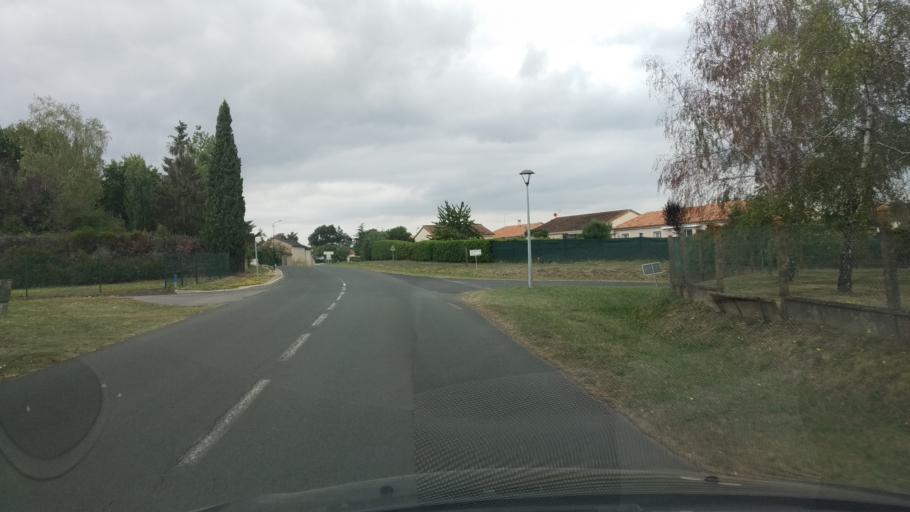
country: FR
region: Poitou-Charentes
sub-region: Departement de la Vienne
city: Smarves
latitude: 46.5072
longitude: 0.3591
